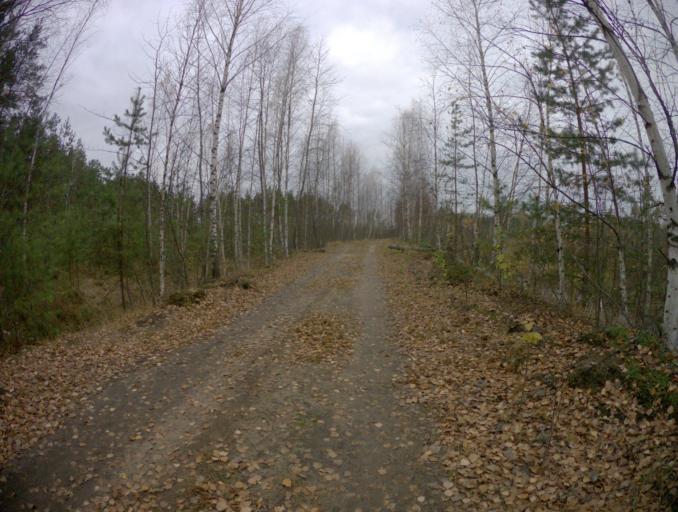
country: RU
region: Moskovskaya
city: Malaya Dubna
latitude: 55.9417
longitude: 38.9578
